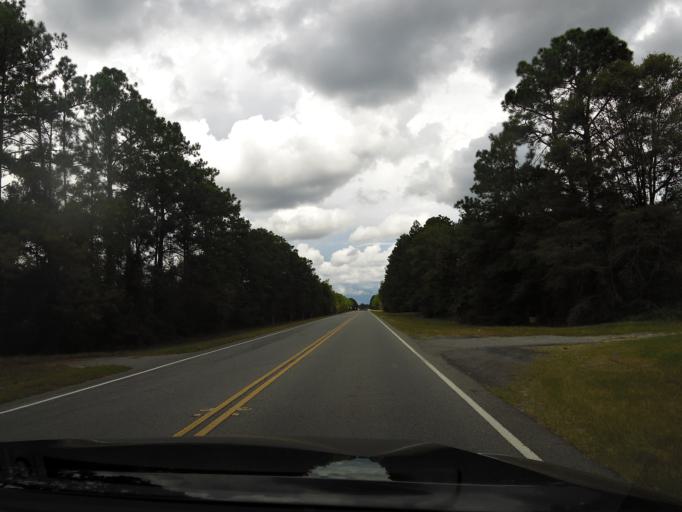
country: US
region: Georgia
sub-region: Brantley County
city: Nahunta
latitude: 31.1762
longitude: -81.9887
